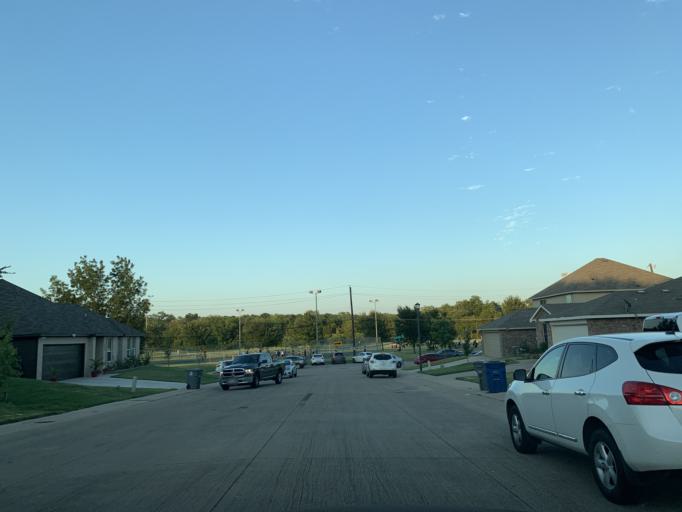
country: US
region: Texas
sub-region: Dallas County
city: Hutchins
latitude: 32.6702
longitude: -96.7951
